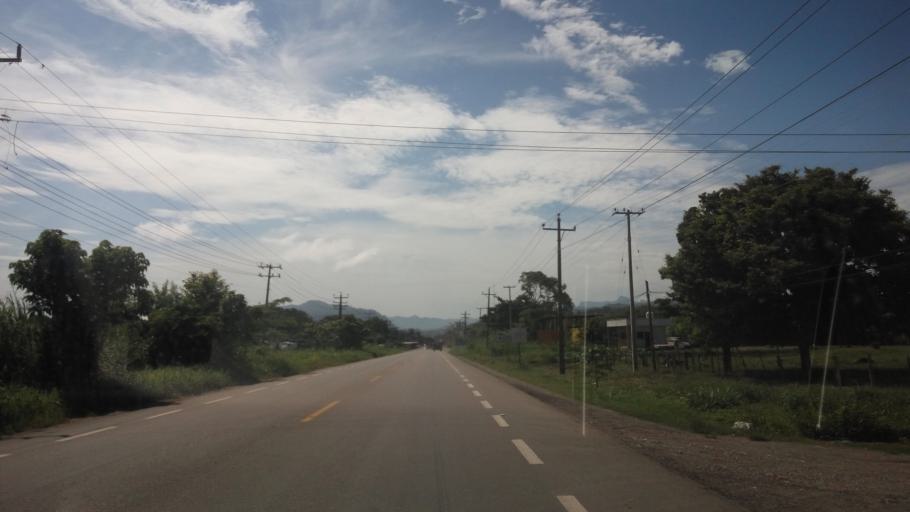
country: MX
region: Tabasco
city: Teapa
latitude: 17.5765
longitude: -92.9594
